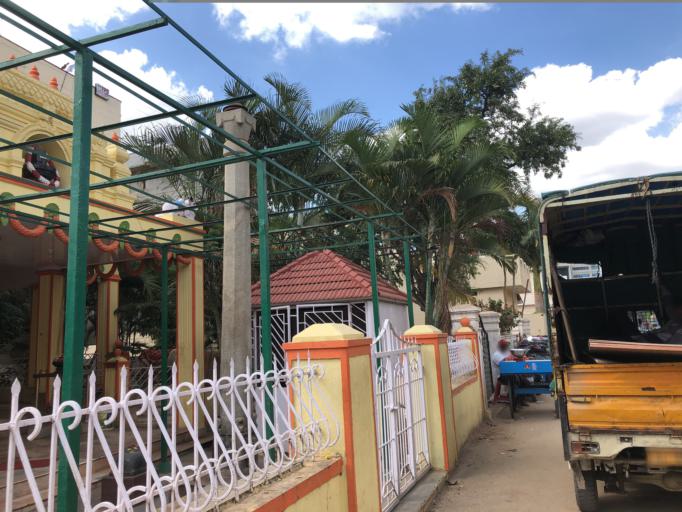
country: IN
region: Karnataka
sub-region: Bangalore Urban
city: Bangalore
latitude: 12.9933
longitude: 77.7014
